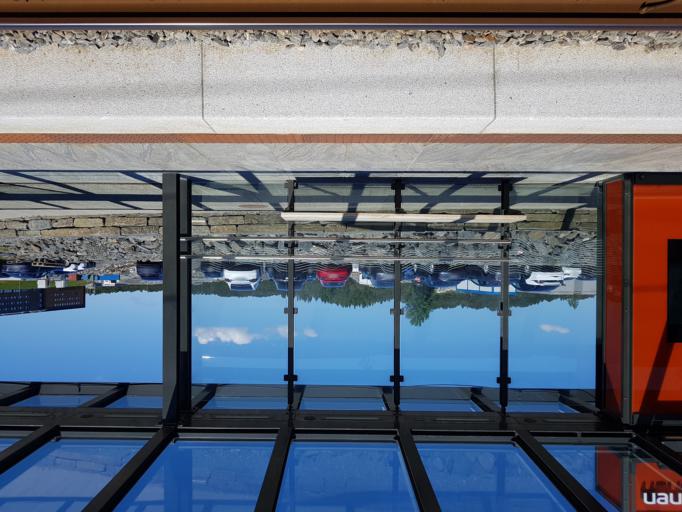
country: NO
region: Hordaland
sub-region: Bergen
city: Ytrebygda
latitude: 60.2903
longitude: 5.2393
